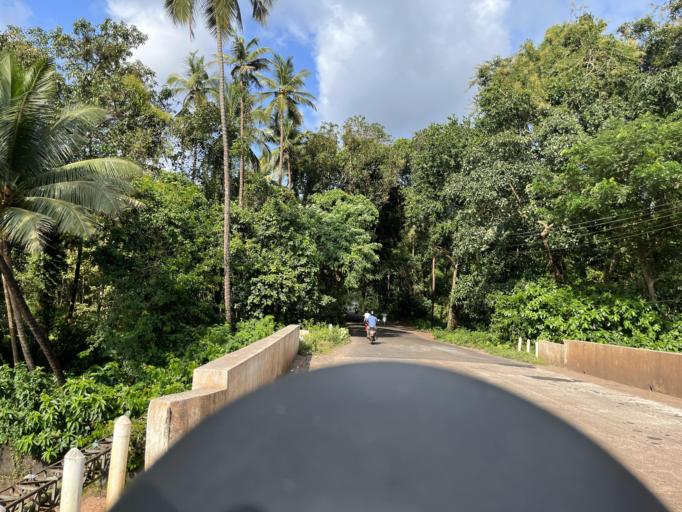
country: IN
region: Goa
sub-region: North Goa
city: Ponda
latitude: 15.4070
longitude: 74.0192
